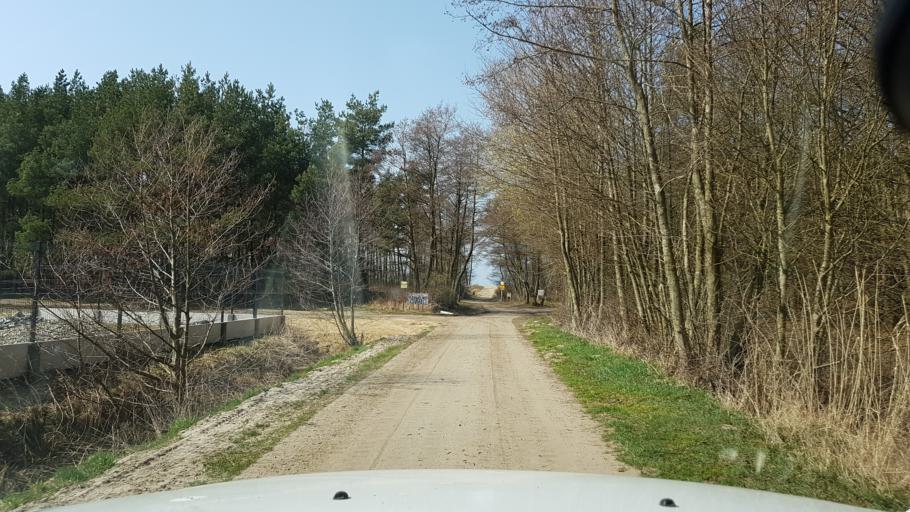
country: PL
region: West Pomeranian Voivodeship
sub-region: Powiat slawienski
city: Darlowo
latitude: 54.4637
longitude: 16.4126
